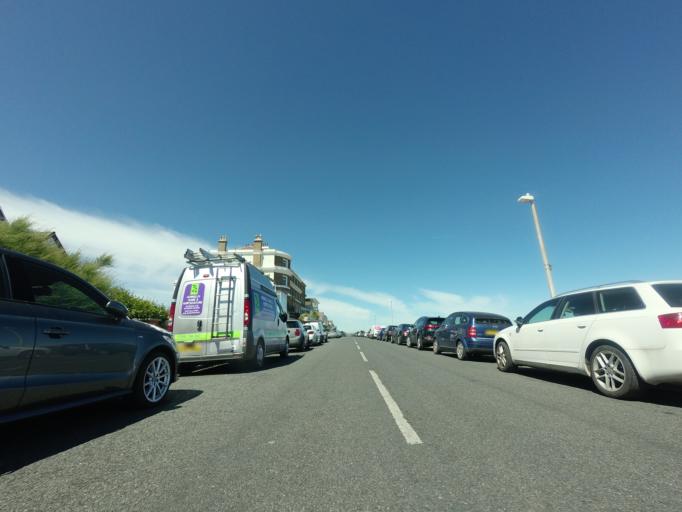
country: GB
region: England
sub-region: Kent
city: Deal
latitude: 51.2321
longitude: 1.4042
